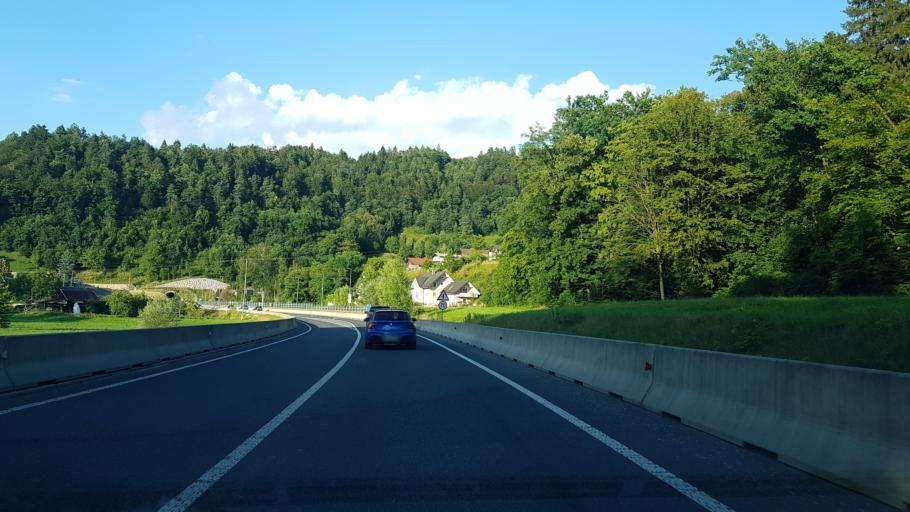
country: SI
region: Skofja Loka
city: Skofja Loka
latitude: 46.1558
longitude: 14.3078
